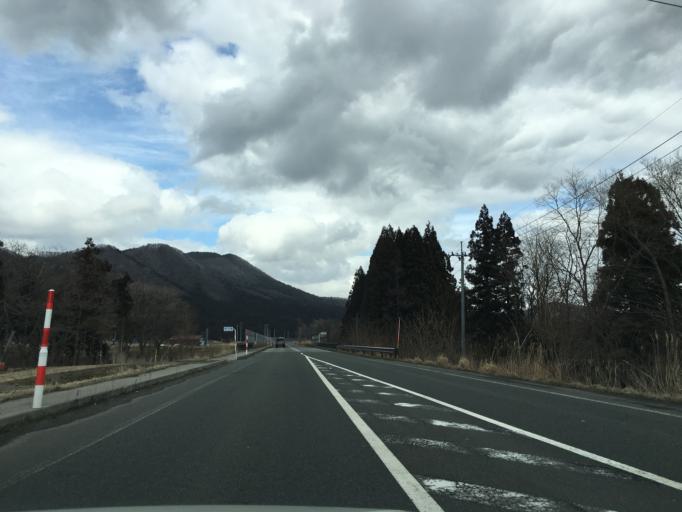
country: JP
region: Akita
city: Hanawa
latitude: 40.2254
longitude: 140.6782
